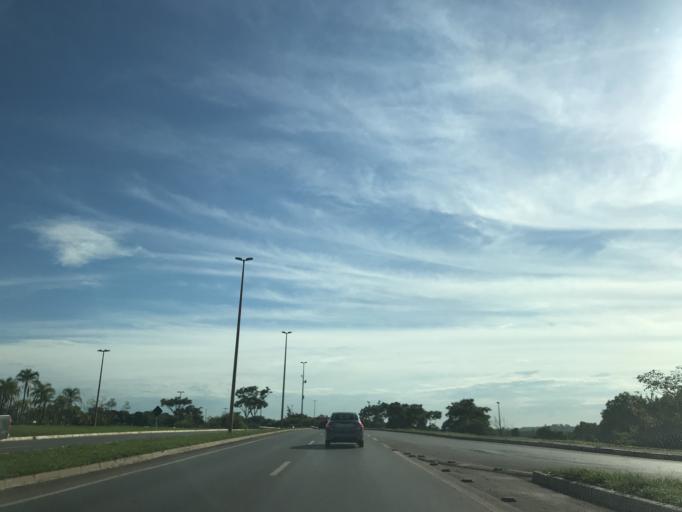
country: BR
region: Federal District
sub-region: Brasilia
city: Brasilia
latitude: -15.8629
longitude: -47.9583
